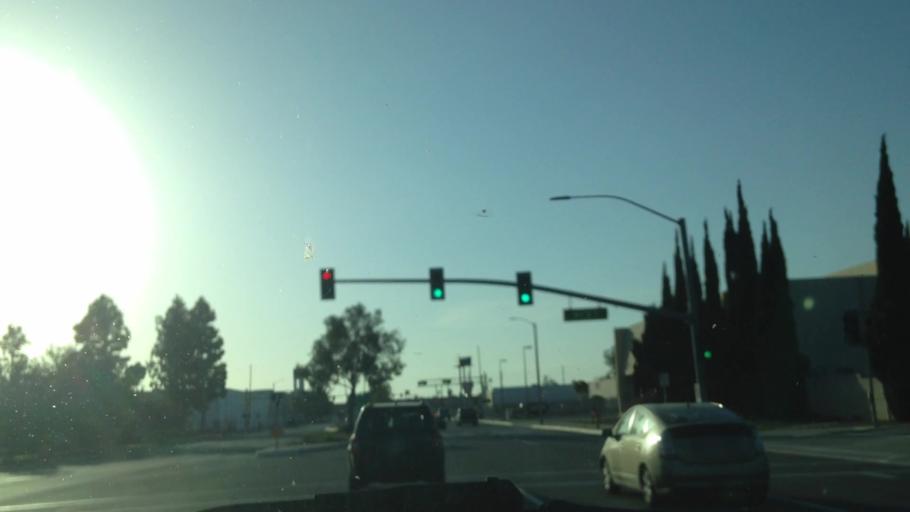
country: US
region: California
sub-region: Orange County
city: Tustin
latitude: 33.7230
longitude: -117.8293
